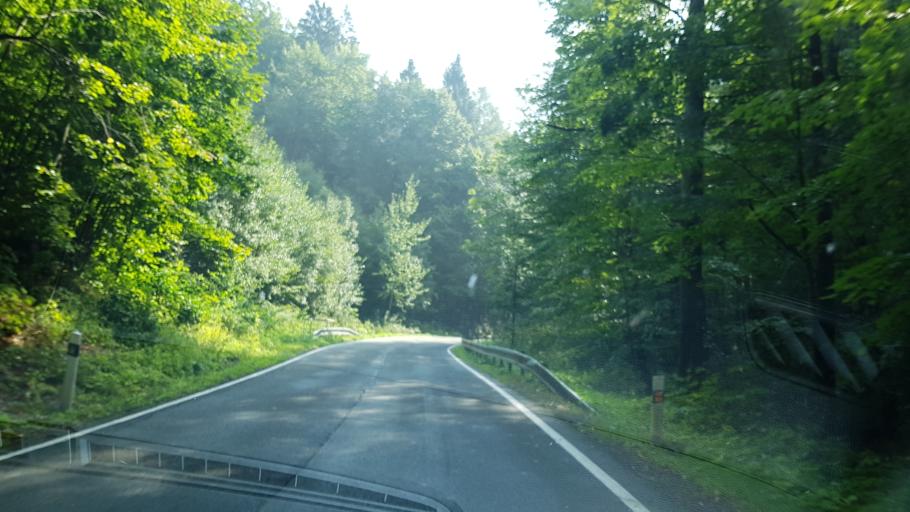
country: CZ
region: Olomoucky
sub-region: Okres Jesenik
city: Jesenik
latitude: 50.2055
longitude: 17.2369
